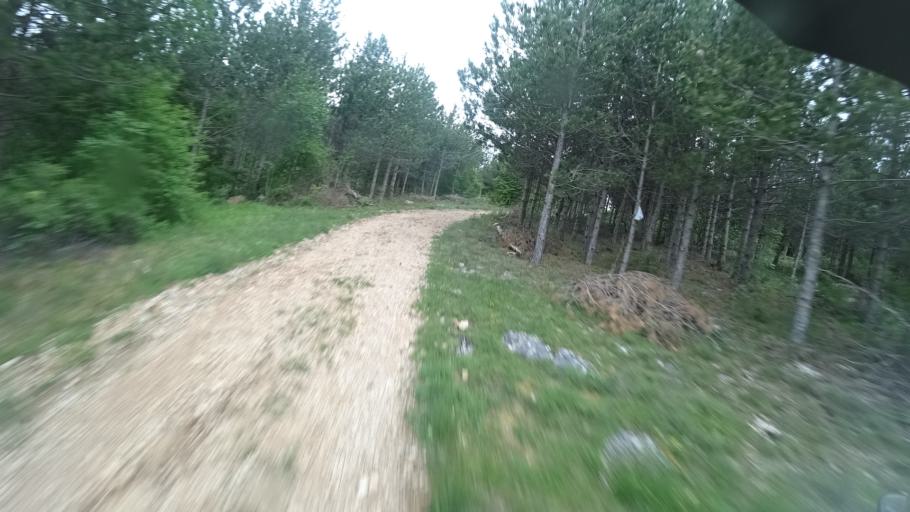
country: HR
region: Sibensko-Kniniska
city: Knin
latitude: 43.9854
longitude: 16.3355
